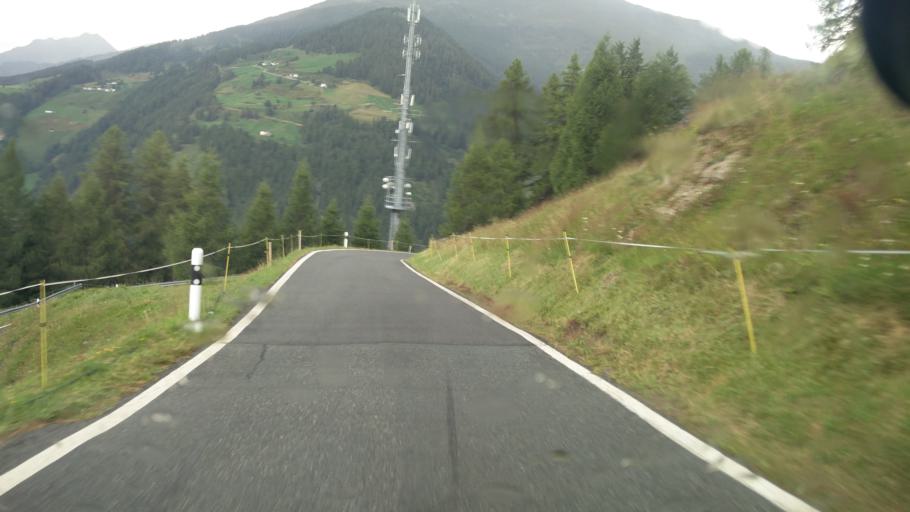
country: IT
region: Trentino-Alto Adige
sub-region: Bolzano
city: Tubre
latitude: 46.5937
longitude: 10.4298
